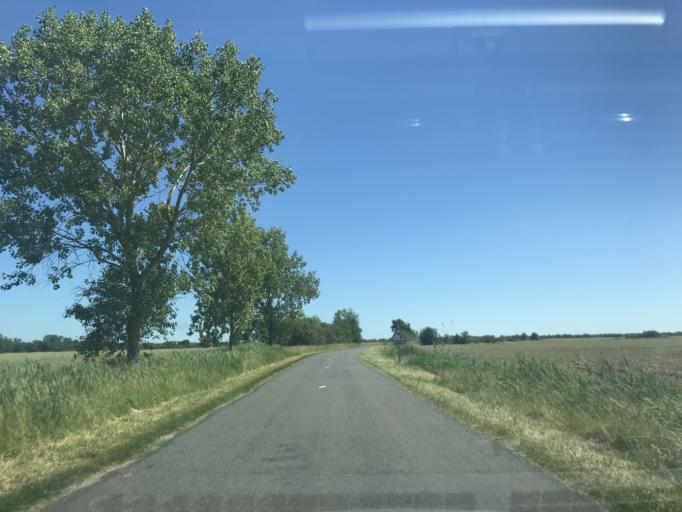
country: FR
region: Poitou-Charentes
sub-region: Departement de la Charente-Maritime
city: Mortagne-sur-Gironde
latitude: 45.4513
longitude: -0.7641
